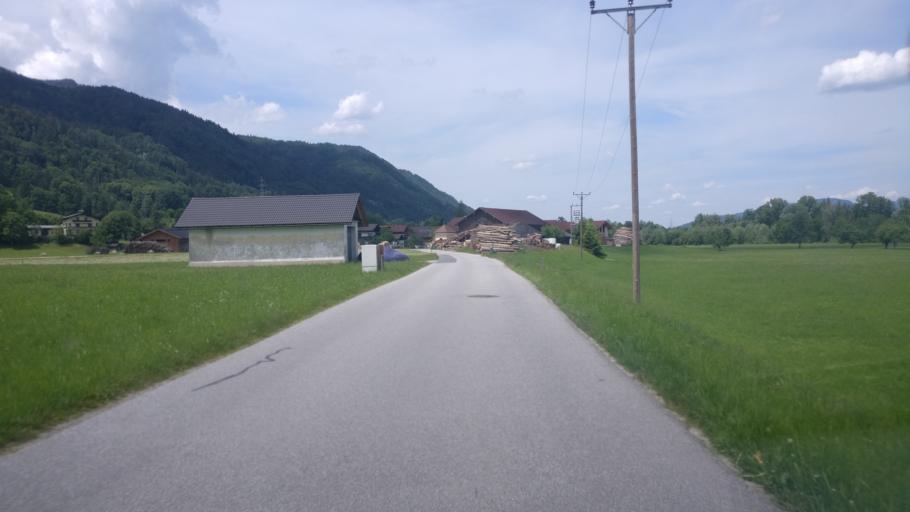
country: AT
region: Salzburg
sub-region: Politischer Bezirk Hallein
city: Kuchl
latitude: 47.6286
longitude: 13.1364
